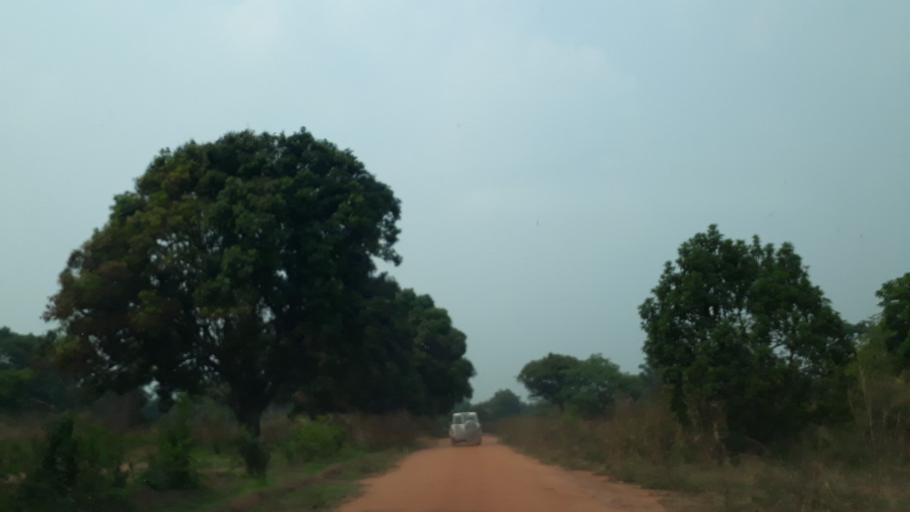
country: CD
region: Kasai-Occidental
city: Tshikapa
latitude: -6.4804
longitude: 20.4364
